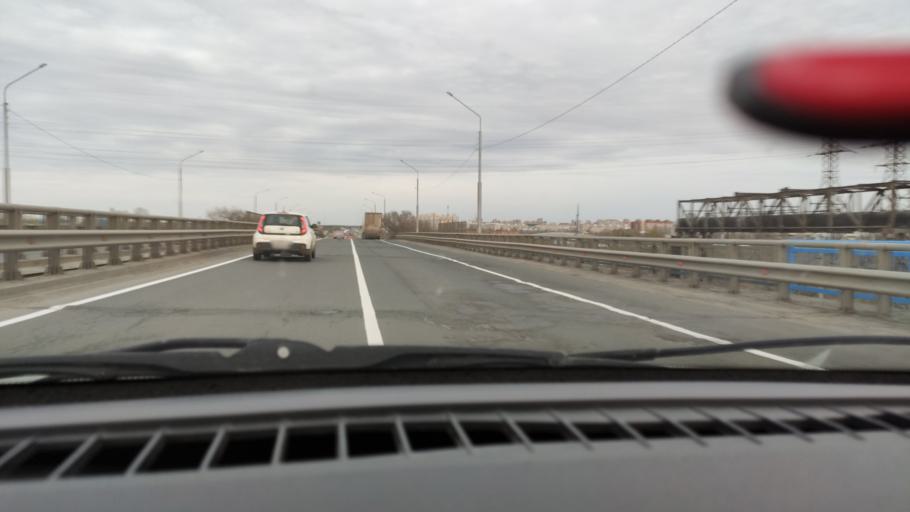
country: RU
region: Orenburg
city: Orenburg
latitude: 51.8524
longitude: 55.1396
